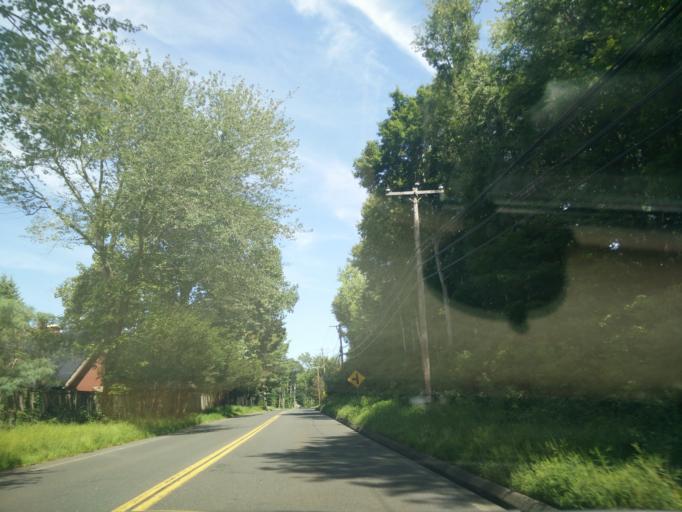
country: US
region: Connecticut
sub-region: New Haven County
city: Madison
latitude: 41.3616
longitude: -72.5659
